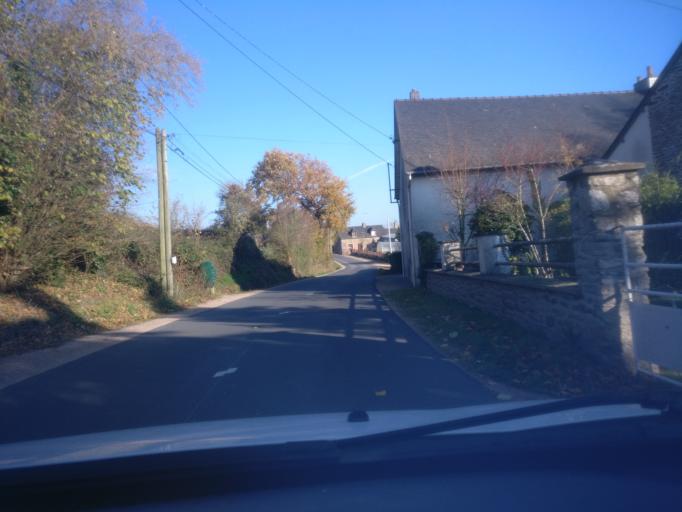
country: FR
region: Brittany
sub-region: Departement d'Ille-et-Vilaine
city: Guichen
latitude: 48.0052
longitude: -1.7920
